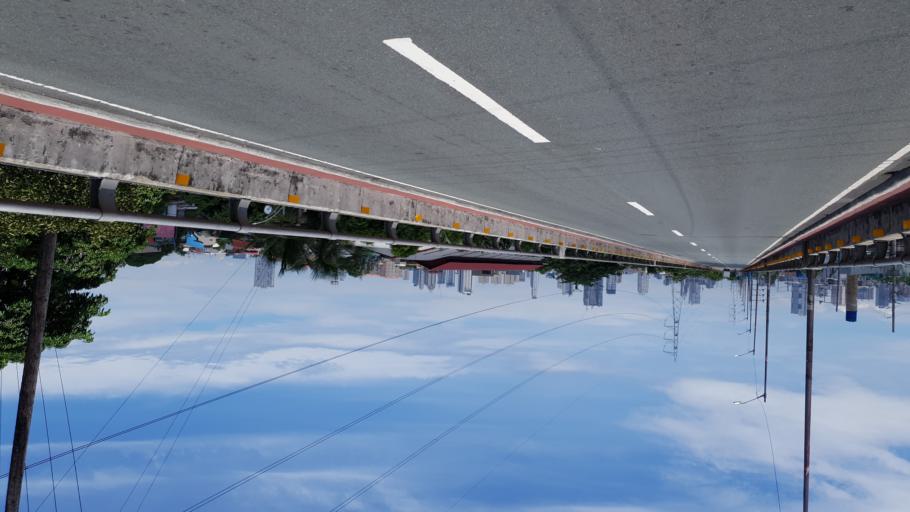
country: PH
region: Metro Manila
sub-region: San Juan
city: San Juan
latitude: 14.5912
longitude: 121.0097
